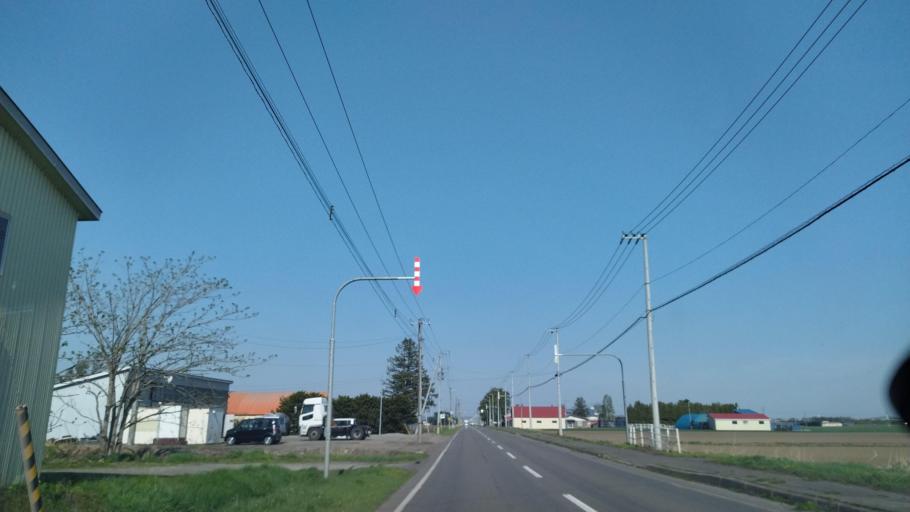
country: JP
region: Hokkaido
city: Obihiro
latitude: 42.9438
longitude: 143.0882
